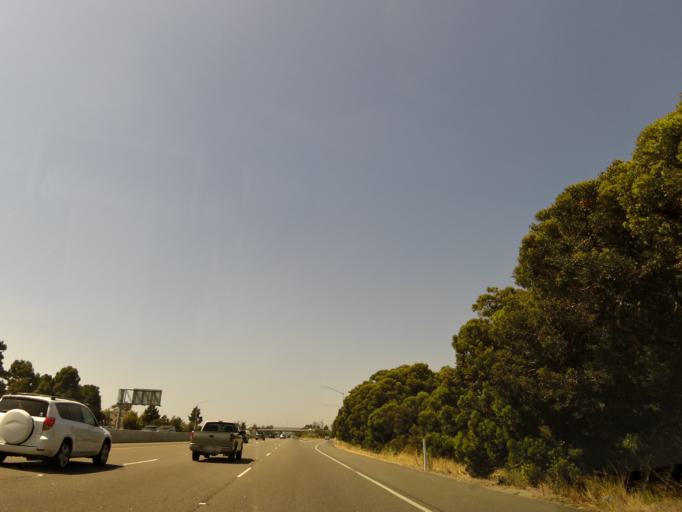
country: US
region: California
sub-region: Santa Barbara County
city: Santa Maria
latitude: 34.9633
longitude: -120.4202
